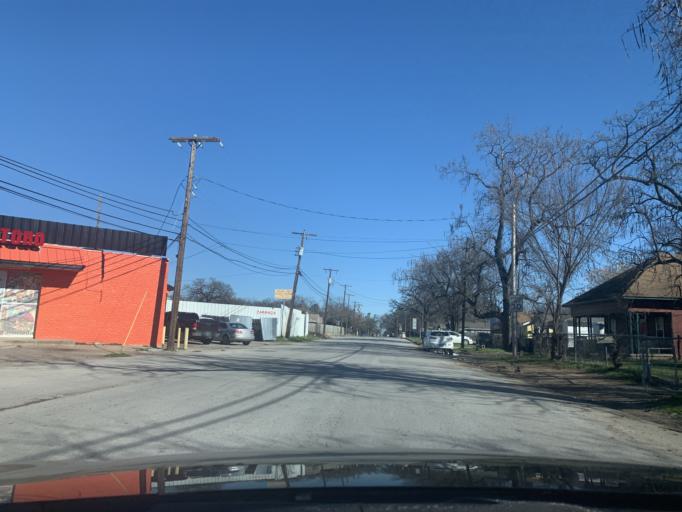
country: US
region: Texas
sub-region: Tarrant County
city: Haltom City
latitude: 32.7818
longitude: -97.2892
